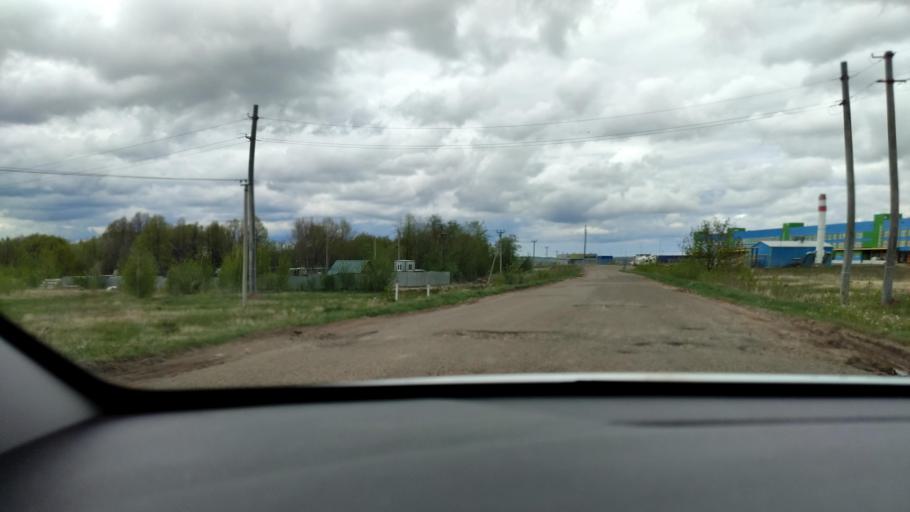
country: RU
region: Tatarstan
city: Vysokaya Gora
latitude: 55.8021
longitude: 49.3128
